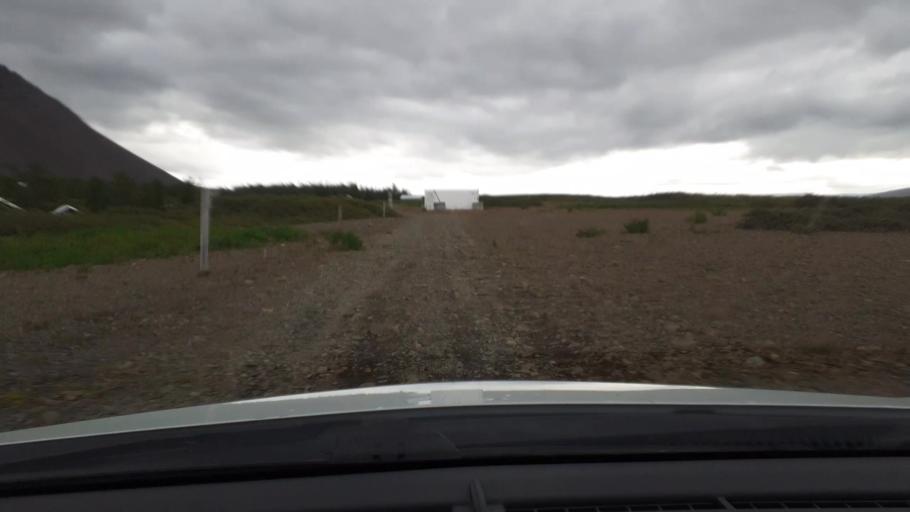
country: IS
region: West
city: Borgarnes
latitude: 64.4597
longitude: -21.9555
